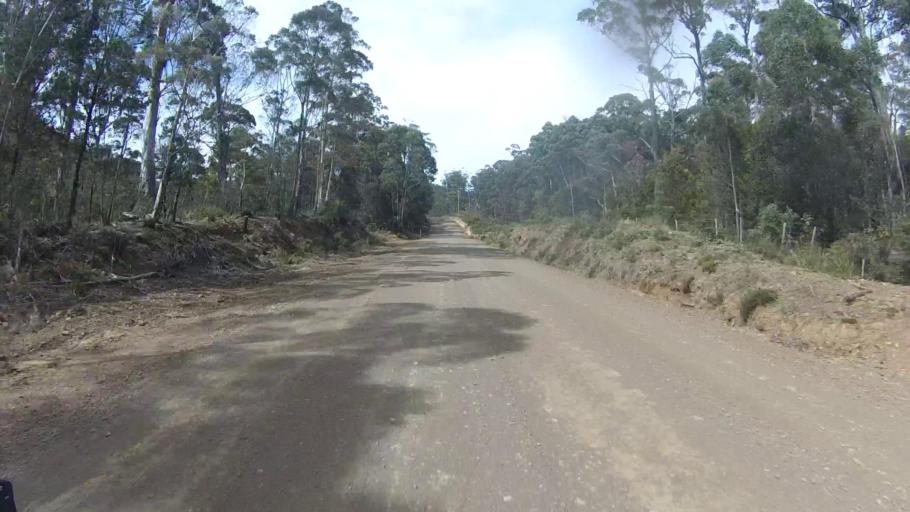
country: AU
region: Tasmania
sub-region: Sorell
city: Sorell
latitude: -42.6807
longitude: 147.8817
